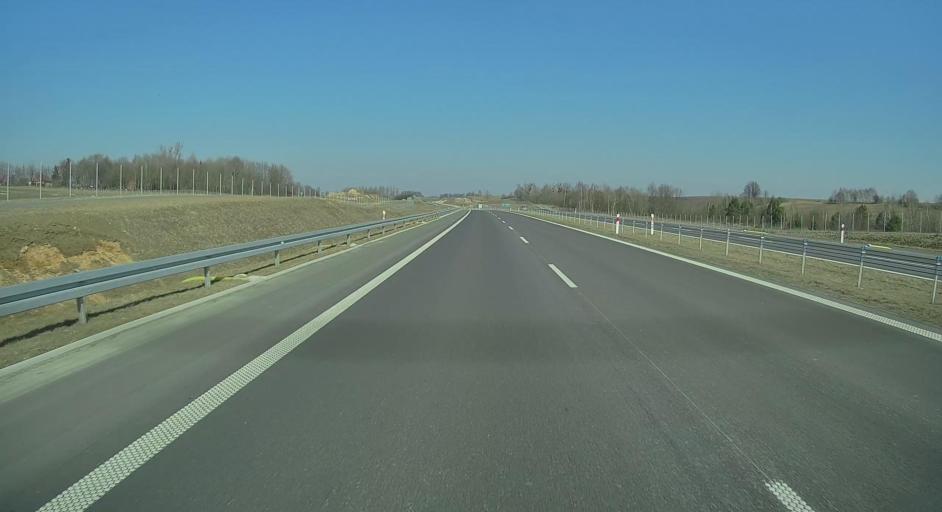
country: PL
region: Lublin Voivodeship
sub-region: Powiat krasnicki
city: Szastarka
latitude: 50.8077
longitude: 22.2993
